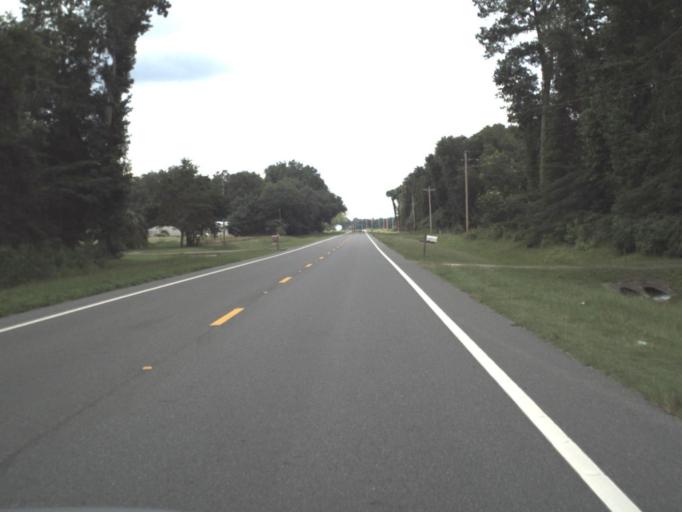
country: US
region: Florida
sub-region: Alachua County
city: Alachua
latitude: 29.8401
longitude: -82.3647
